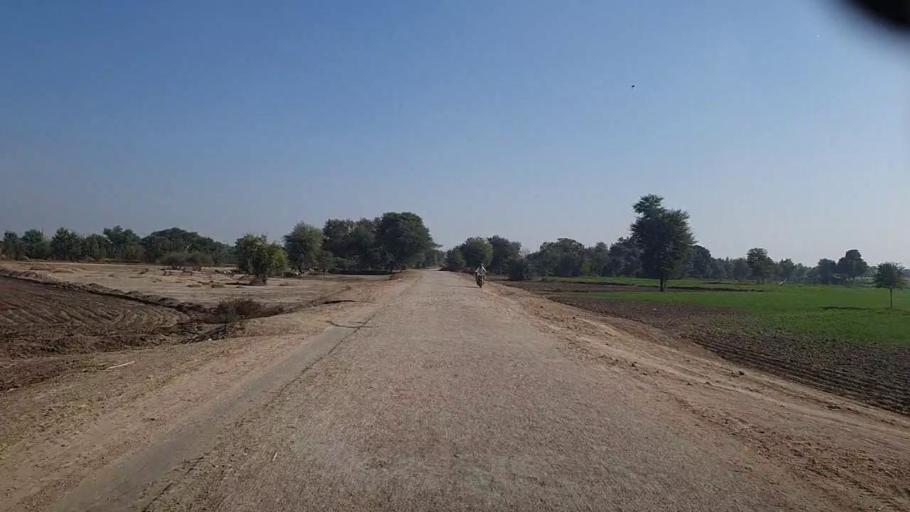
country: PK
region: Sindh
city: Darya Khan Marri
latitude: 26.6646
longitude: 68.3381
